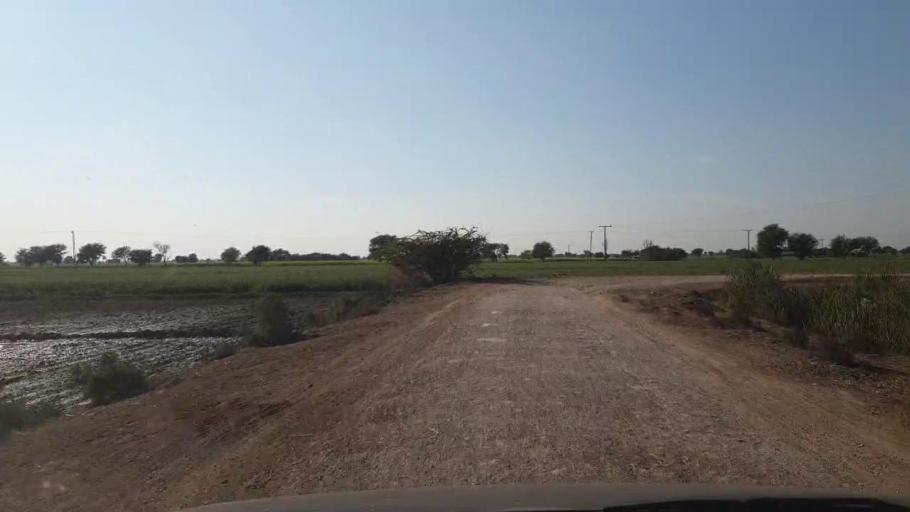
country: PK
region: Sindh
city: Shahpur Chakar
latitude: 26.1691
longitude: 68.6814
